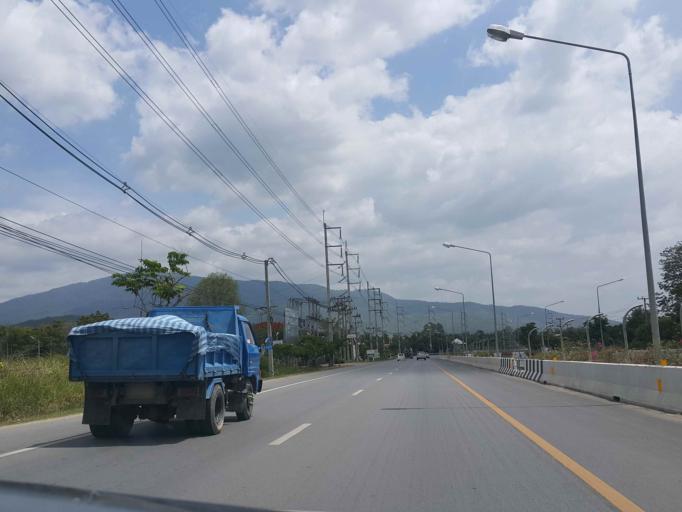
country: TH
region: Chiang Mai
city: Hang Dong
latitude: 18.7313
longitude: 98.9263
